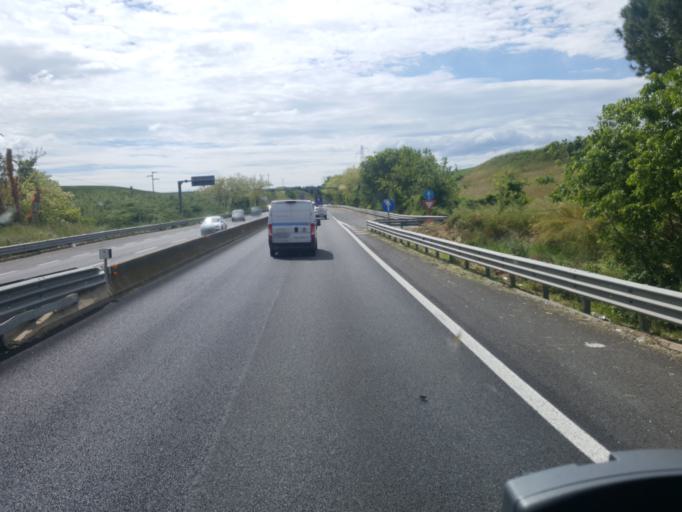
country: IT
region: Latium
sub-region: Citta metropolitana di Roma Capitale
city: La Massimina-Casal Lumbroso
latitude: 41.8857
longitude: 12.3260
